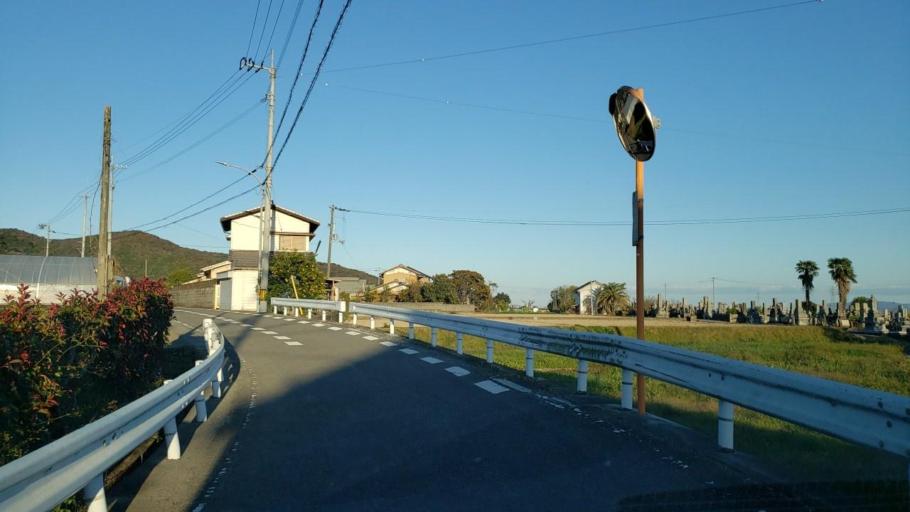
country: JP
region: Tokushima
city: Kamojimacho-jogejima
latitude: 34.0957
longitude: 134.2929
